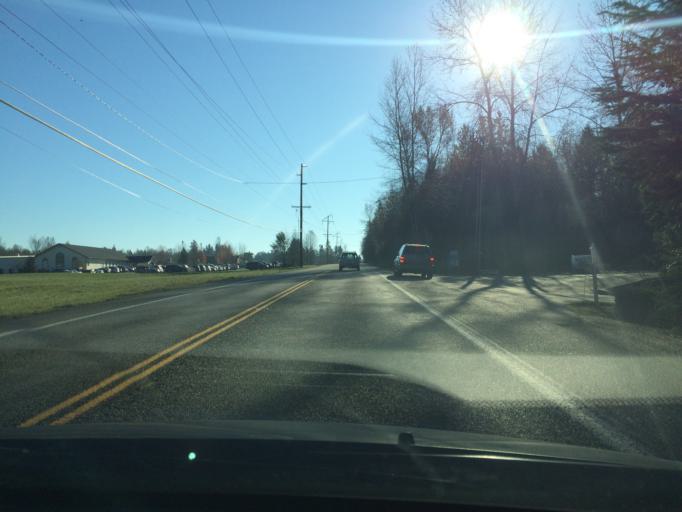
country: US
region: Washington
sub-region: Whatcom County
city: Bellingham
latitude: 48.8395
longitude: -122.4431
